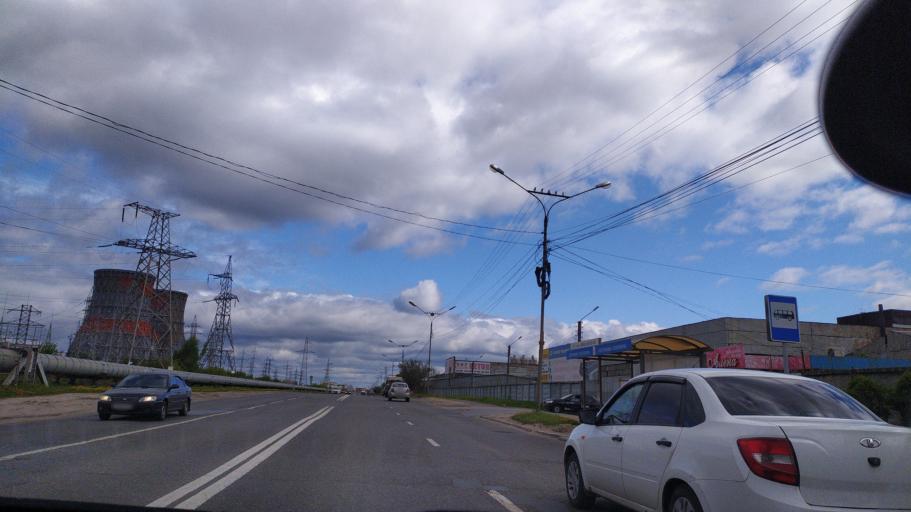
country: RU
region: Chuvashia
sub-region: Cheboksarskiy Rayon
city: Cheboksary
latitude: 56.1208
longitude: 47.3030
